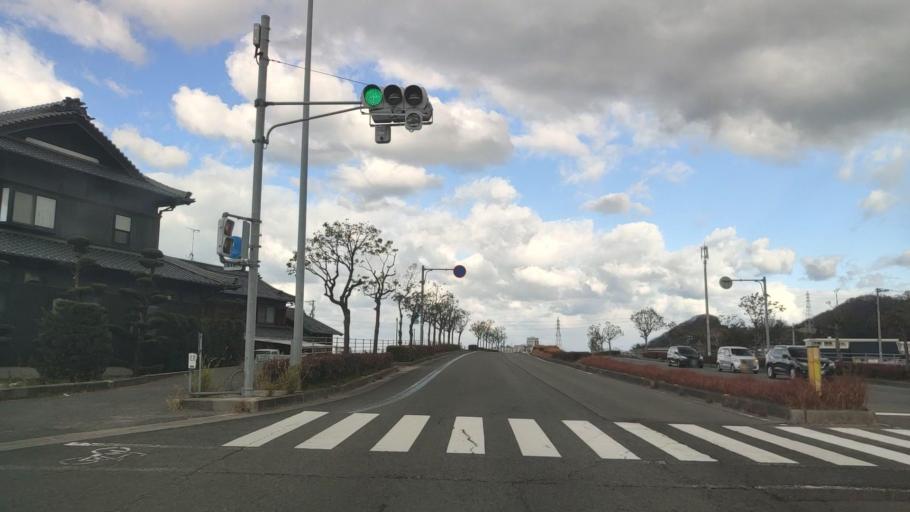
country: JP
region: Ehime
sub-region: Shikoku-chuo Shi
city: Matsuyama
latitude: 33.8990
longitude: 132.7576
